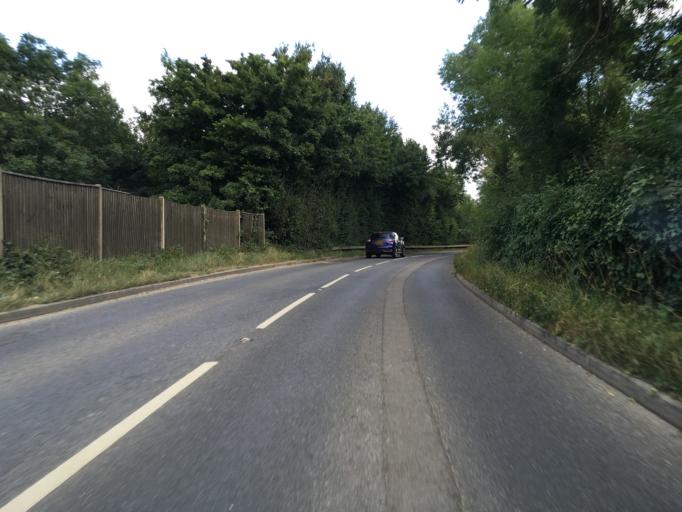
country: GB
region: England
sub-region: Kent
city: Headcorn
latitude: 51.1660
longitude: 0.6338
